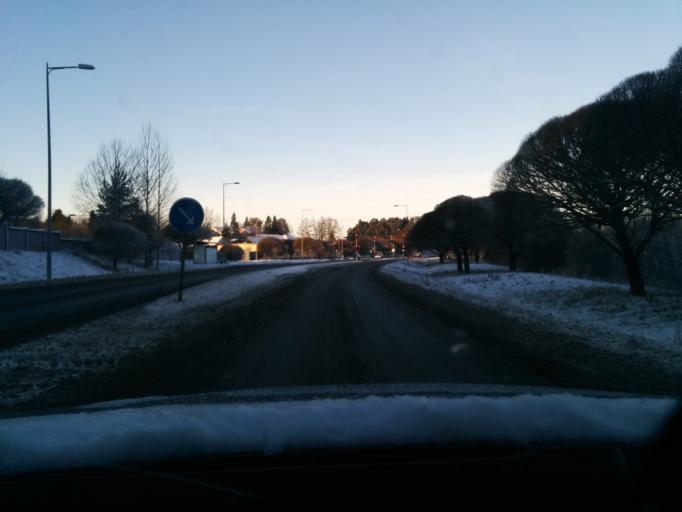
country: SE
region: Stockholm
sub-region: Taby Kommun
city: Taby
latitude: 59.4669
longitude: 18.0563
